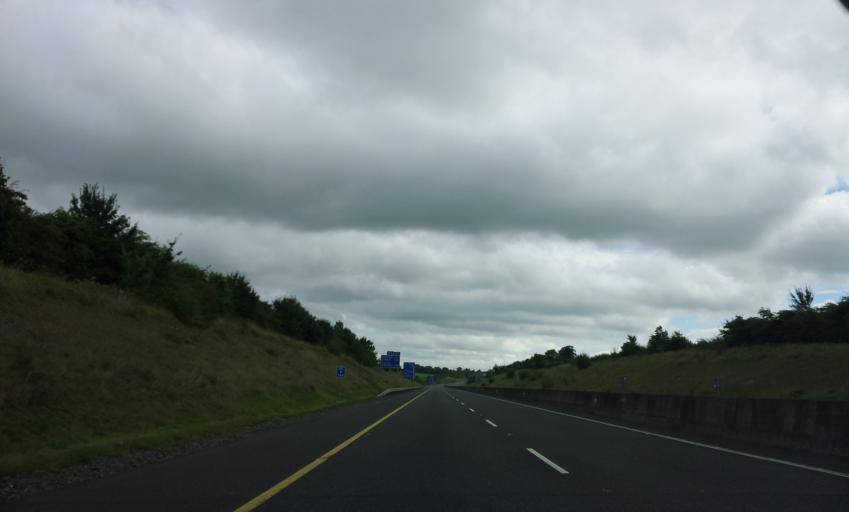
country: IE
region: Munster
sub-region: North Tipperary
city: Nenagh
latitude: 52.8533
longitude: -8.1453
